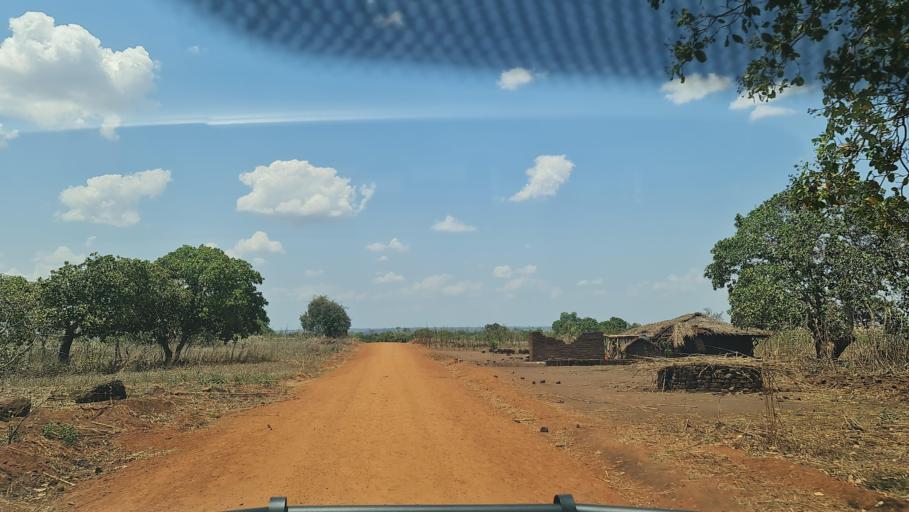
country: MZ
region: Nampula
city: Nacala
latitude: -14.7969
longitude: 40.0693
